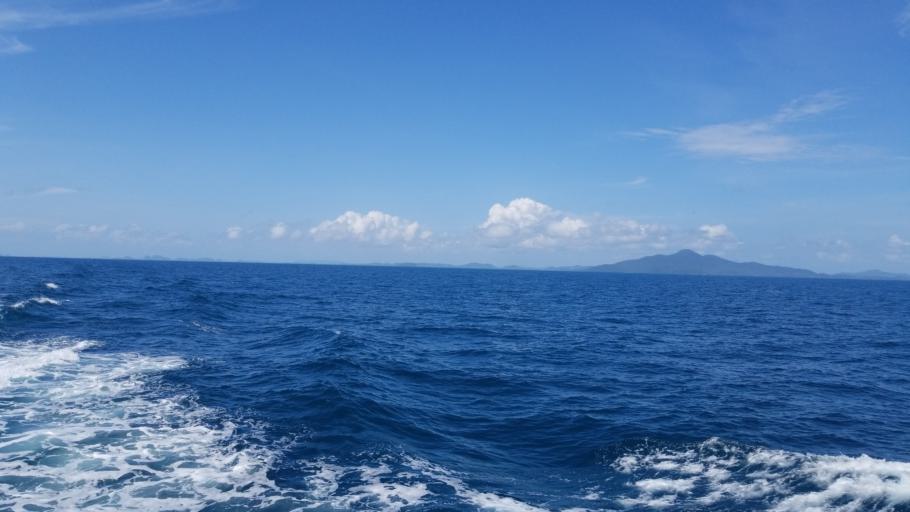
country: TH
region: Phangnga
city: Ban Ao Nang
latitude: 7.8324
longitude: 98.8403
